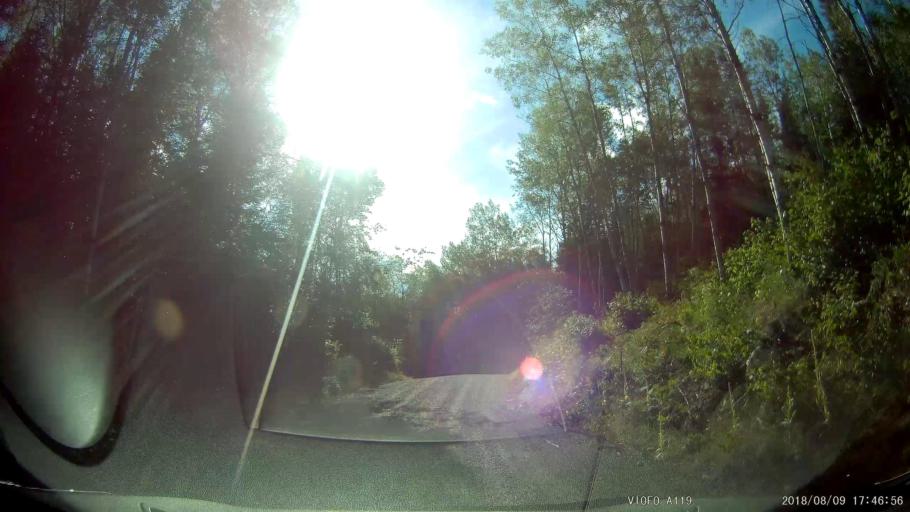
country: CA
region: Ontario
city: Rayside-Balfour
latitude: 46.5935
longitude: -81.5343
